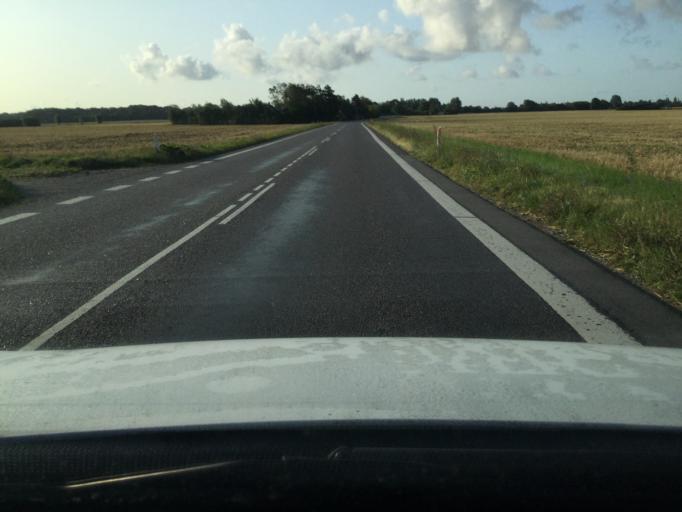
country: DK
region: Zealand
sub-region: Lolland Kommune
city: Nakskov
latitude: 54.7969
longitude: 11.2746
